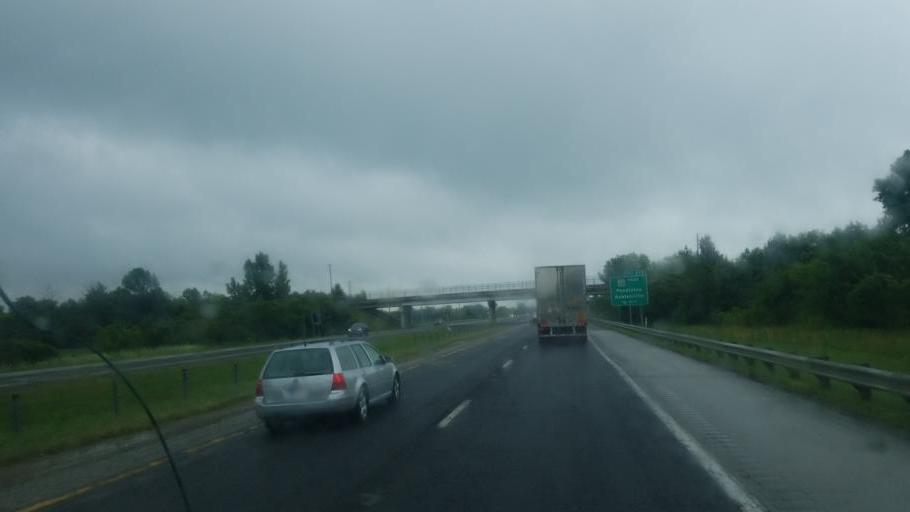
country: US
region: Indiana
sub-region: Madison County
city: Pendleton
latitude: 40.0184
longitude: -85.7645
